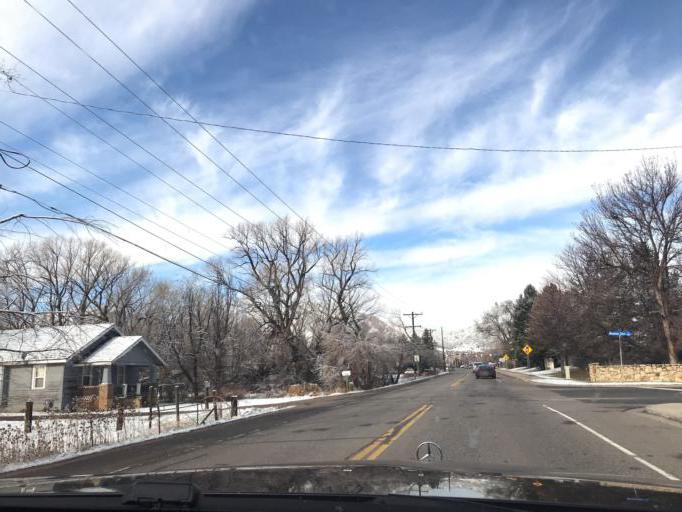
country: US
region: Colorado
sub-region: Boulder County
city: Boulder
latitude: 40.0002
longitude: -105.2221
